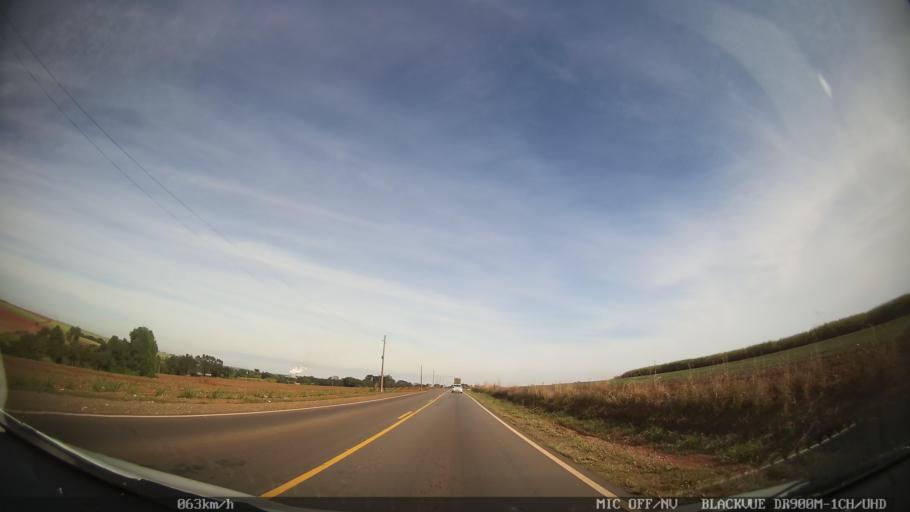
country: BR
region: Sao Paulo
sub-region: Rio Das Pedras
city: Rio das Pedras
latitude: -22.7896
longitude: -47.6409
